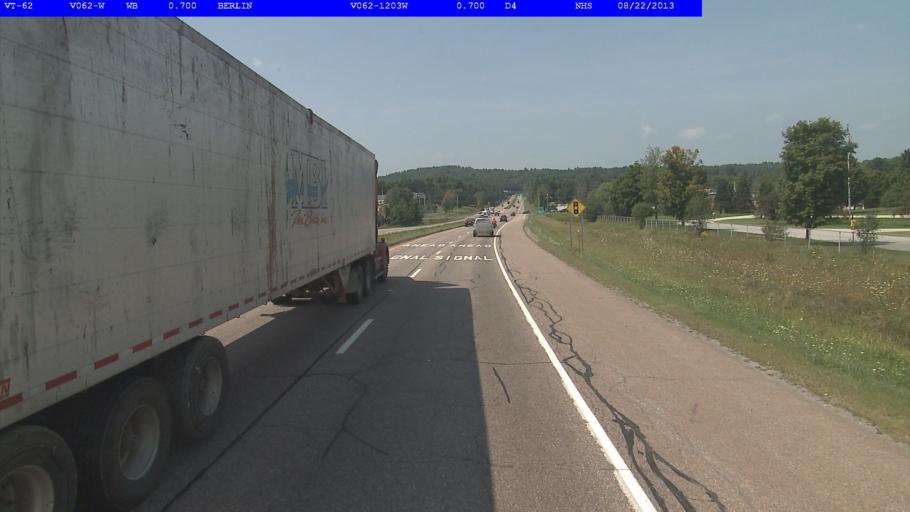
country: US
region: Vermont
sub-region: Washington County
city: Montpelier
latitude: 44.2132
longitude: -72.5708
